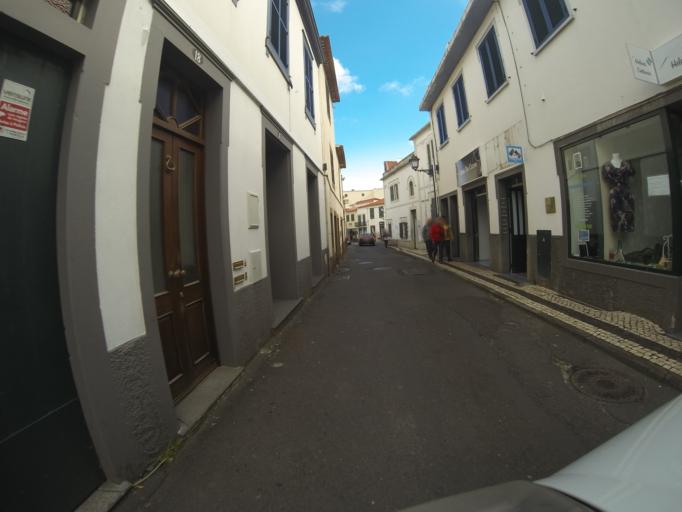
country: PT
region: Madeira
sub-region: Machico
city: Machico
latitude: 32.7186
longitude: -16.7655
